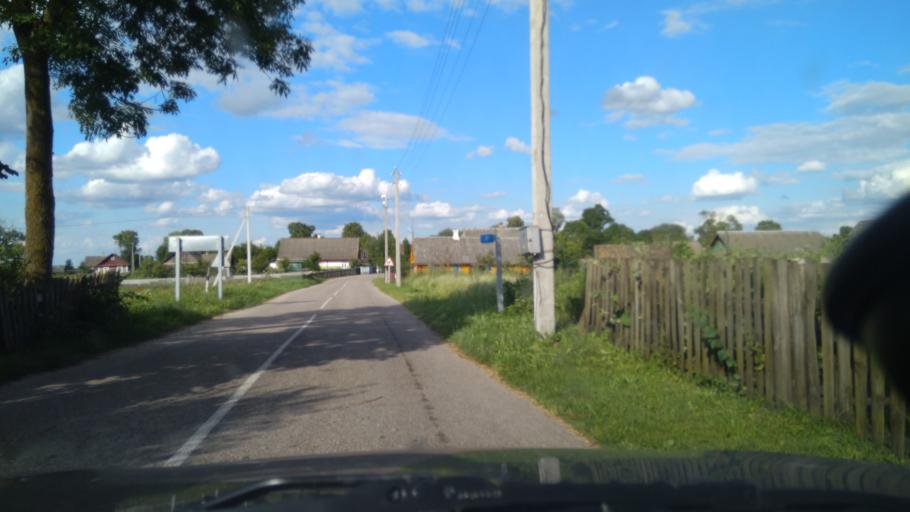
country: BY
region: Grodnenskaya
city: Masty
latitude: 53.3122
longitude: 24.6960
